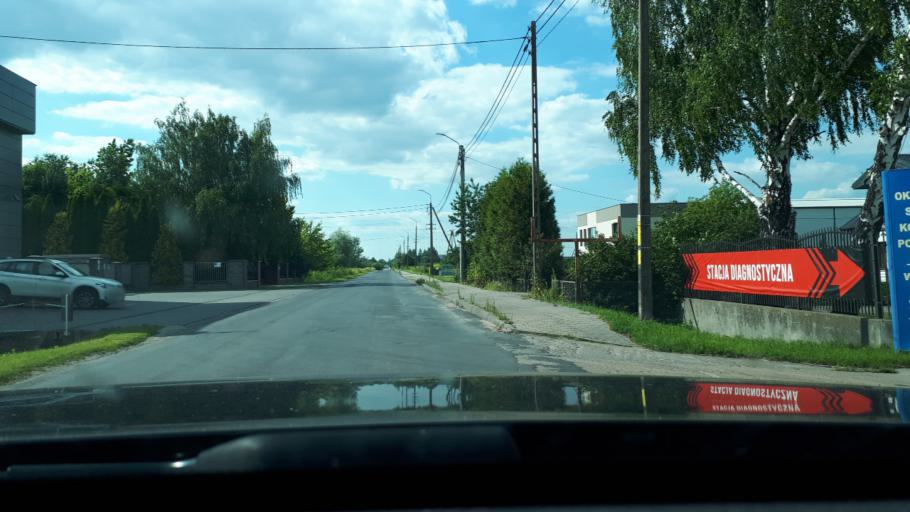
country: PL
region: Masovian Voivodeship
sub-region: Powiat grojecki
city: Warka
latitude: 51.7920
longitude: 21.1762
